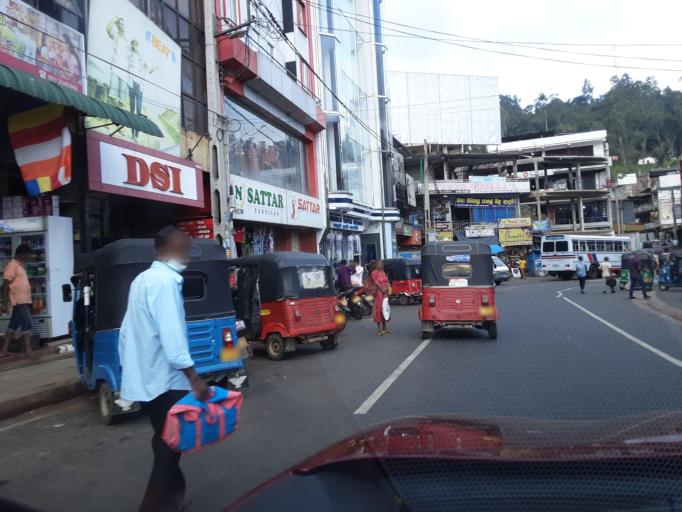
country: LK
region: Central
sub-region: Nuwara Eliya District
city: Nuwara Eliya
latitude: 6.9057
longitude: 80.9118
